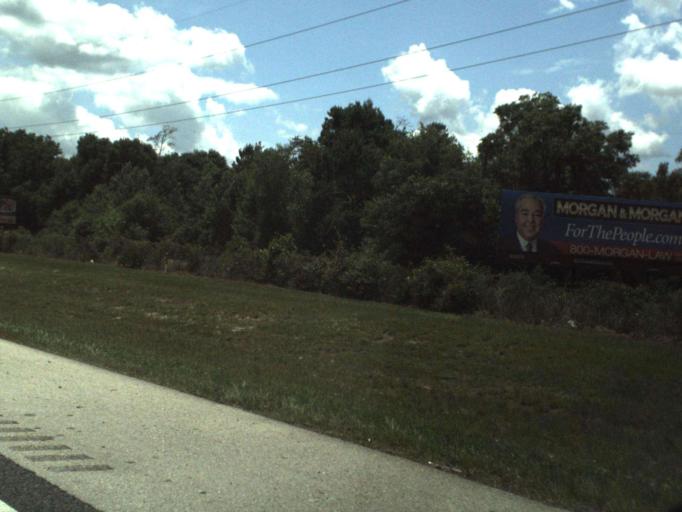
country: US
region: Florida
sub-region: Volusia County
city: Lake Helen
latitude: 29.0076
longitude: -81.2409
